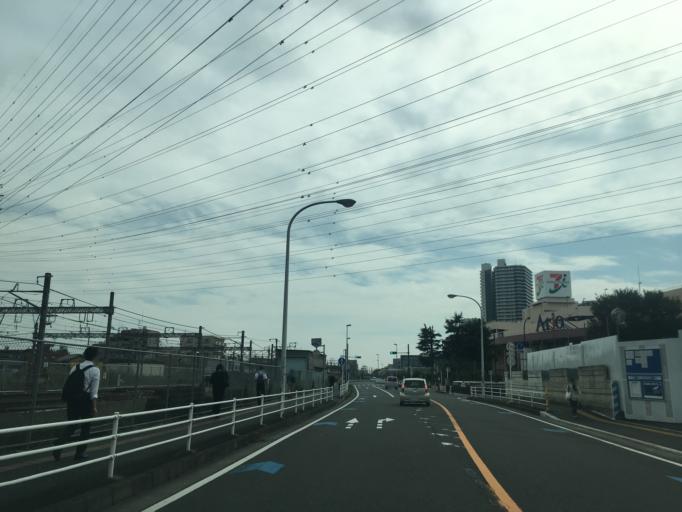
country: JP
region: Tokyo
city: Hachioji
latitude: 35.5932
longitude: 139.3477
